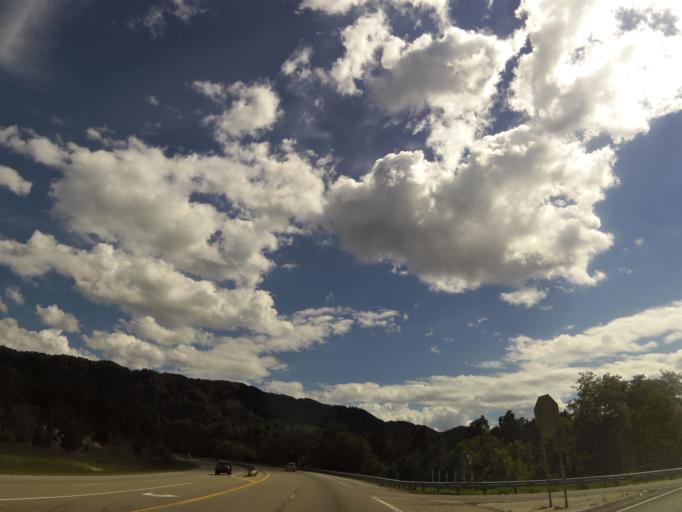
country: US
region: Tennessee
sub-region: Grainger County
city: Rutledge
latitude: 36.3548
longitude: -83.4351
